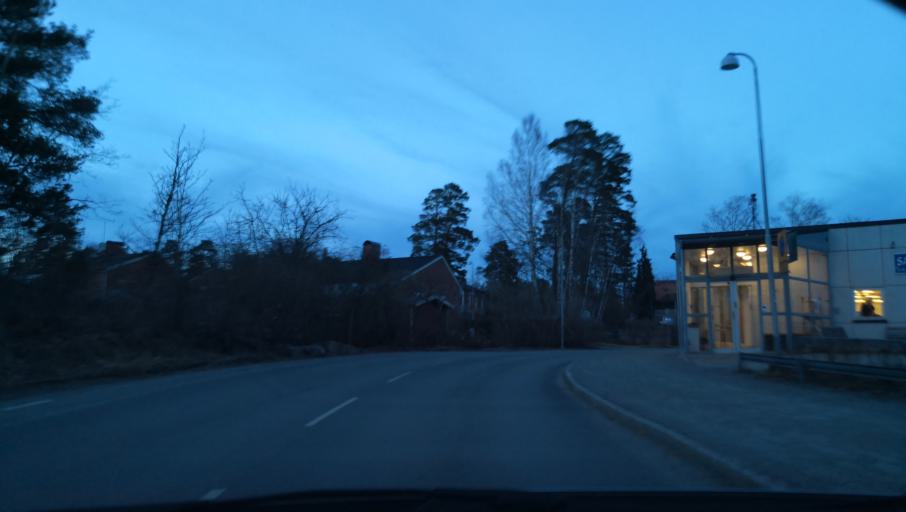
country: SE
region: Stockholm
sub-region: Varmdo Kommun
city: Gustavsberg
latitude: 59.3332
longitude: 18.3889
